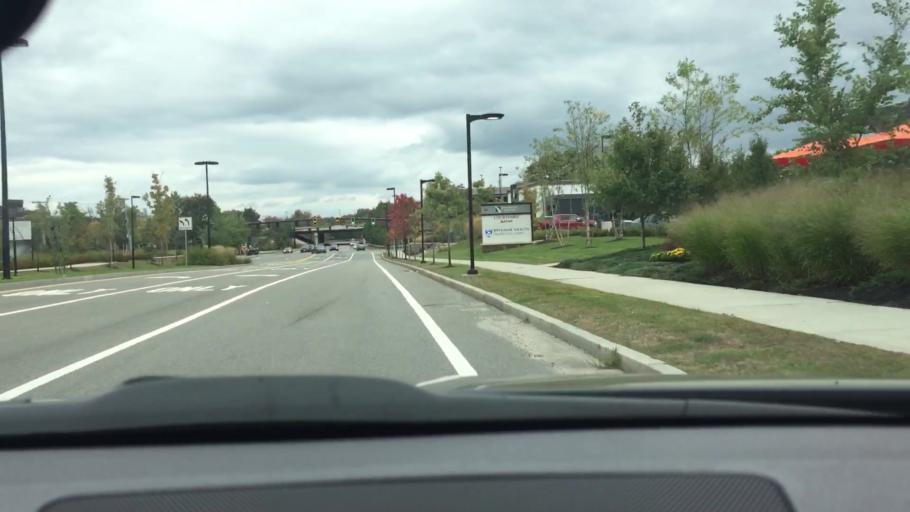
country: US
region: Massachusetts
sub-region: Norfolk County
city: Dedham
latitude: 42.2096
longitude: -71.1505
